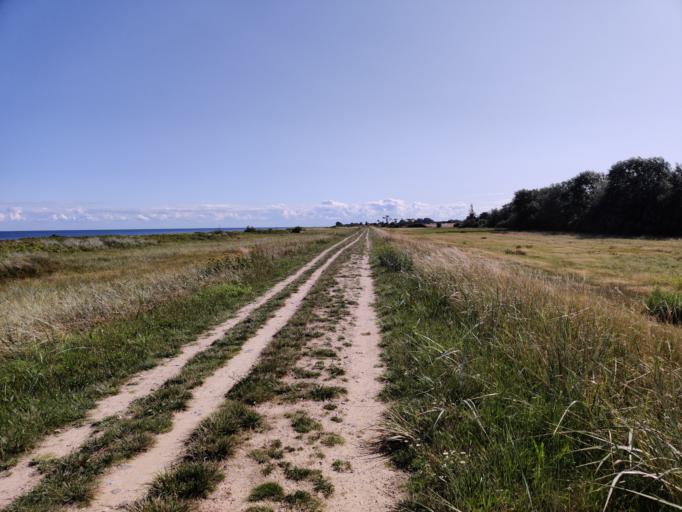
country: DK
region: Zealand
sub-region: Guldborgsund Kommune
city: Nykobing Falster
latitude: 54.5836
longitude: 11.9714
